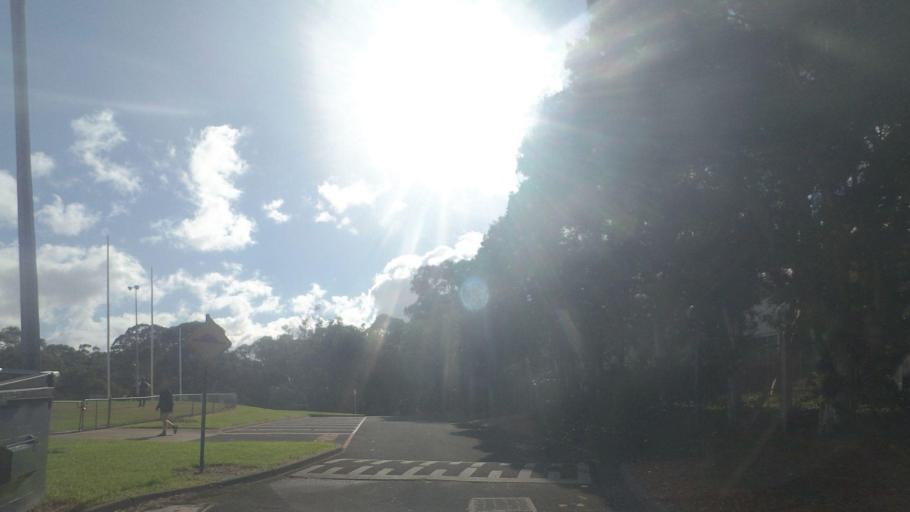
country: AU
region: Victoria
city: Forest Hill
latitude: -37.8371
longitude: 145.1748
